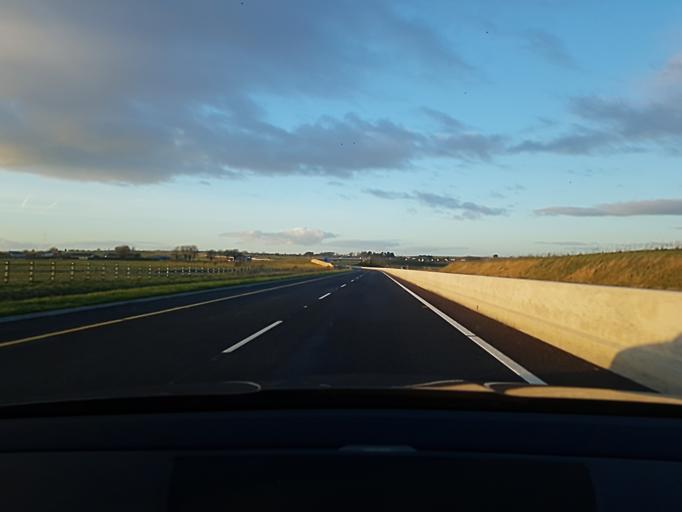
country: IE
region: Connaught
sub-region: County Galway
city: Athenry
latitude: 53.3886
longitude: -8.8016
